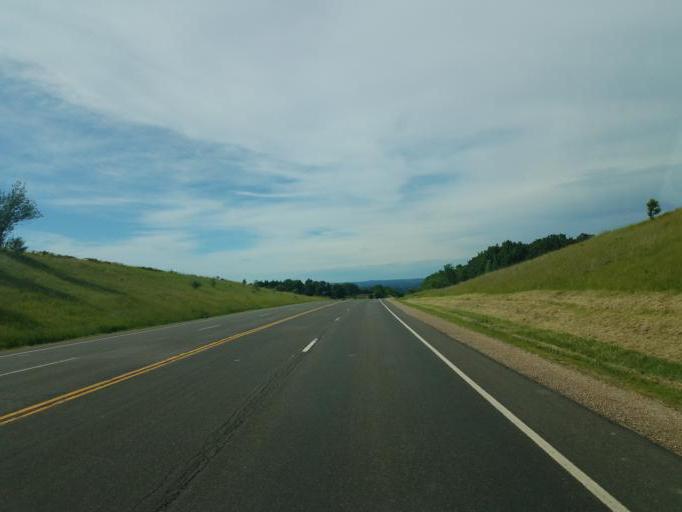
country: US
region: Wisconsin
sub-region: Monroe County
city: Tomah
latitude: 43.8995
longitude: -90.4907
